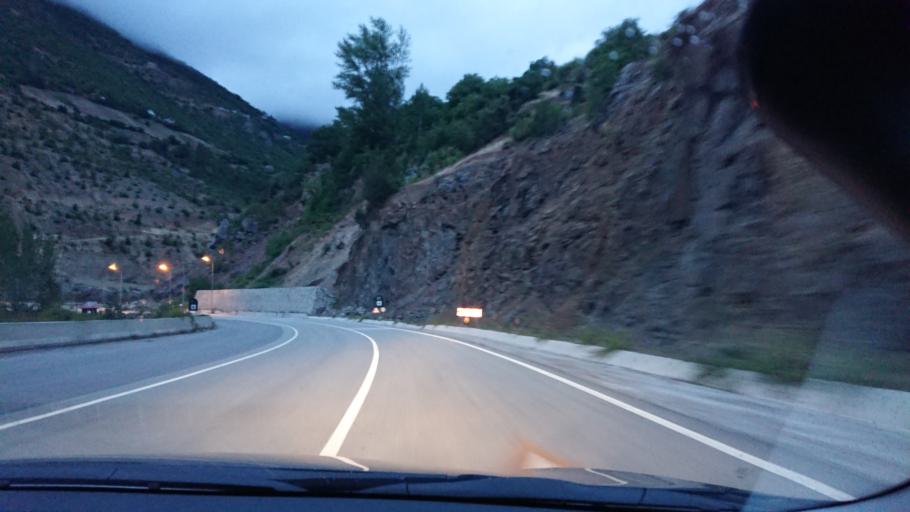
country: TR
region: Gumushane
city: Torul
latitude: 40.6315
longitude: 39.2393
